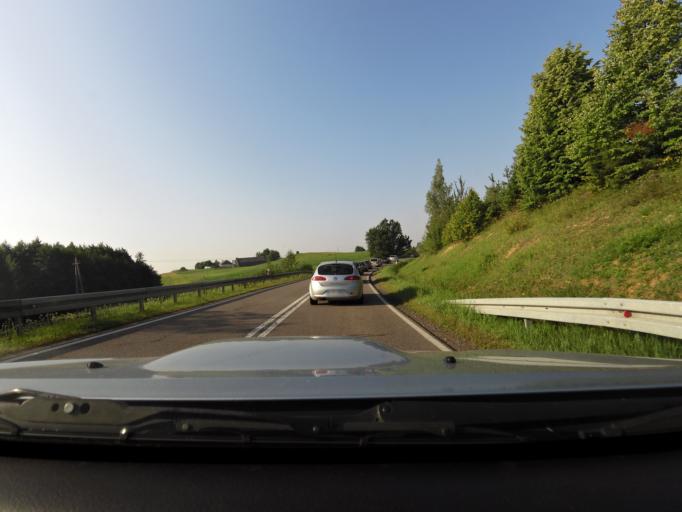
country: PL
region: Podlasie
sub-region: Powiat sejnenski
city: Sejny
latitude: 54.1131
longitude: 23.4234
